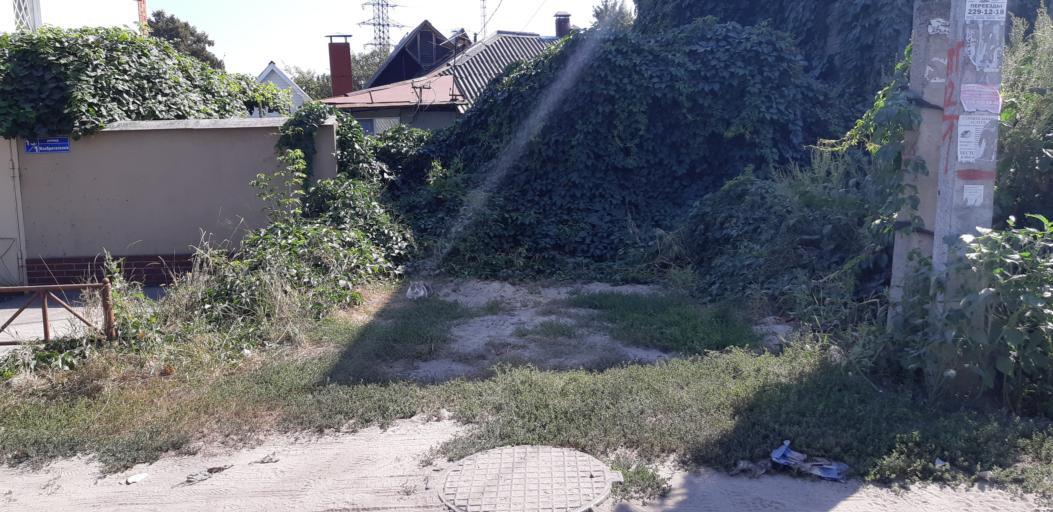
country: RU
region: Voronezj
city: Voronezh
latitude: 51.6663
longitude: 39.1698
